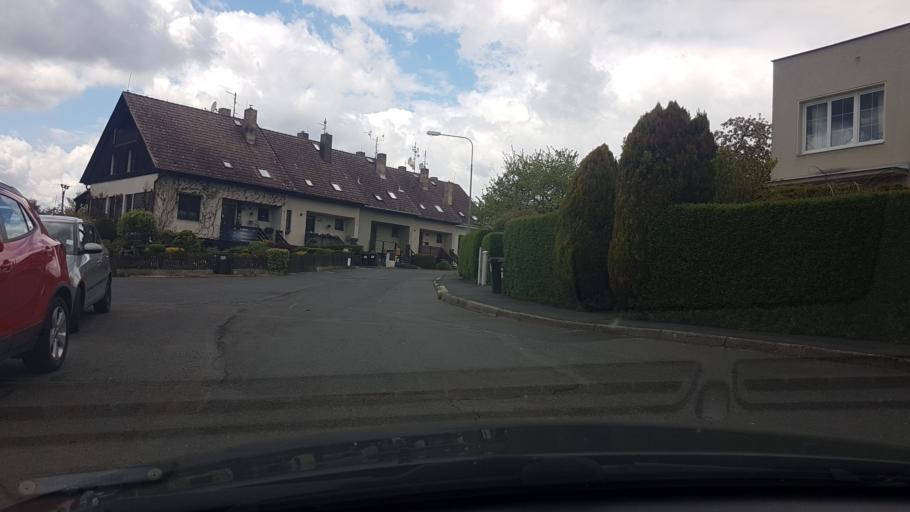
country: CZ
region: Karlovarsky
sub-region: Okres Cheb
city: Cheb
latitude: 50.0607
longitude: 12.3803
